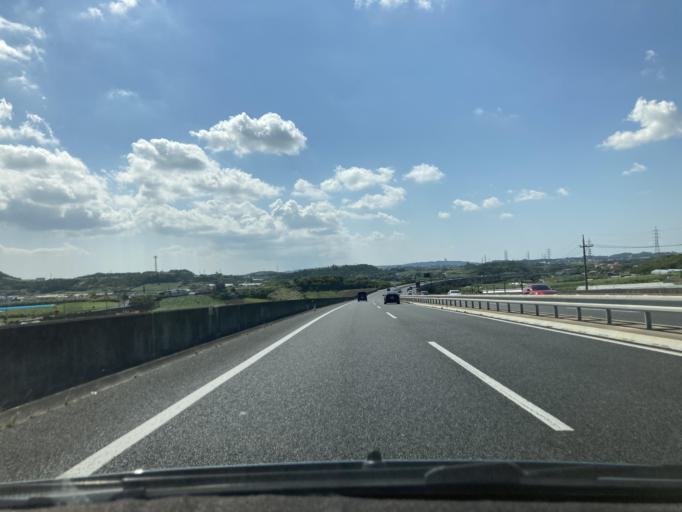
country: JP
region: Okinawa
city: Tomigusuku
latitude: 26.1899
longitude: 127.7385
